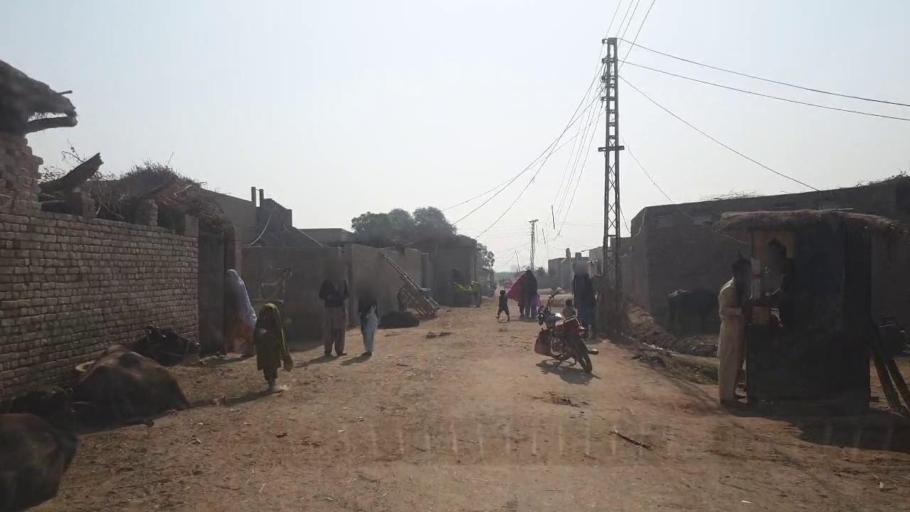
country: PK
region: Sindh
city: Tando Allahyar
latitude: 25.3618
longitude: 68.6498
